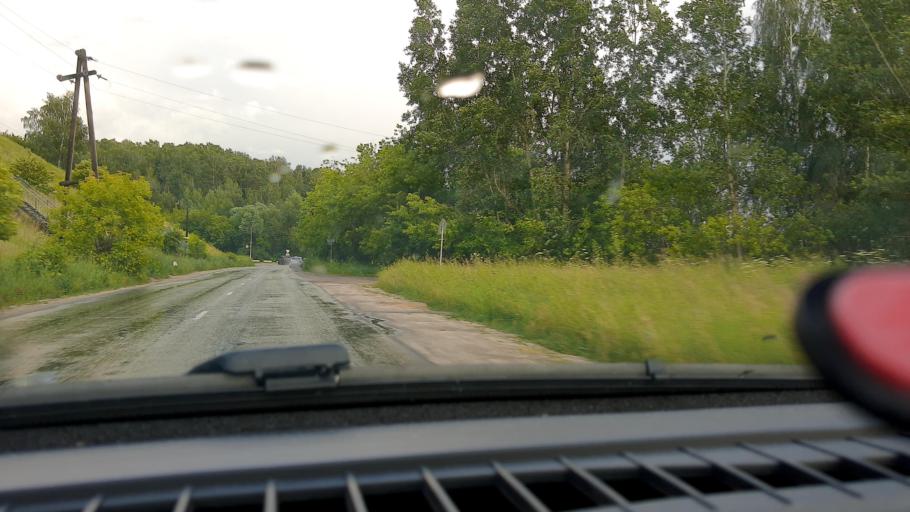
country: RU
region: Nizjnij Novgorod
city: Gorodets
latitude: 56.6685
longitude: 43.4529
